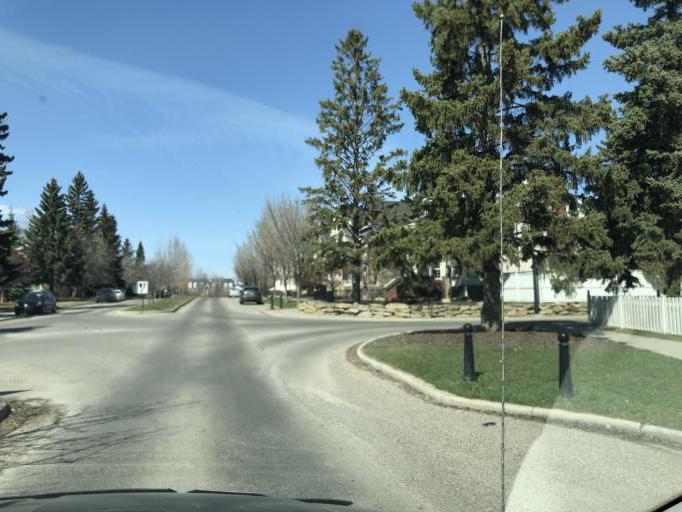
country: CA
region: Alberta
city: Calgary
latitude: 51.0190
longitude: -114.1140
